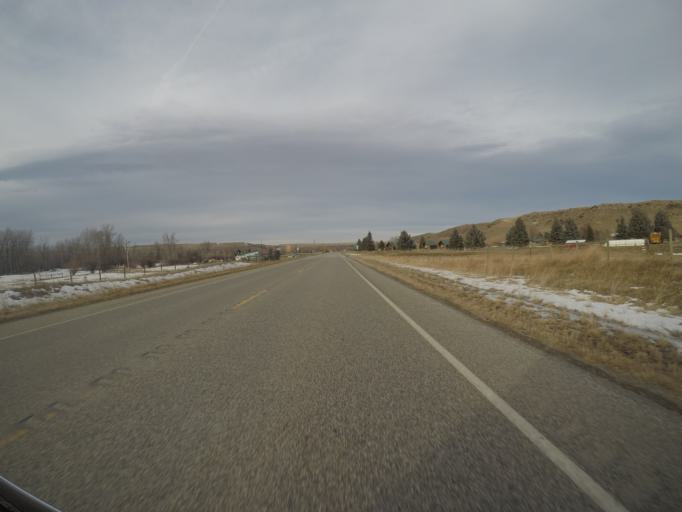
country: US
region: Montana
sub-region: Stillwater County
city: Absarokee
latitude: 45.4784
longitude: -109.4498
